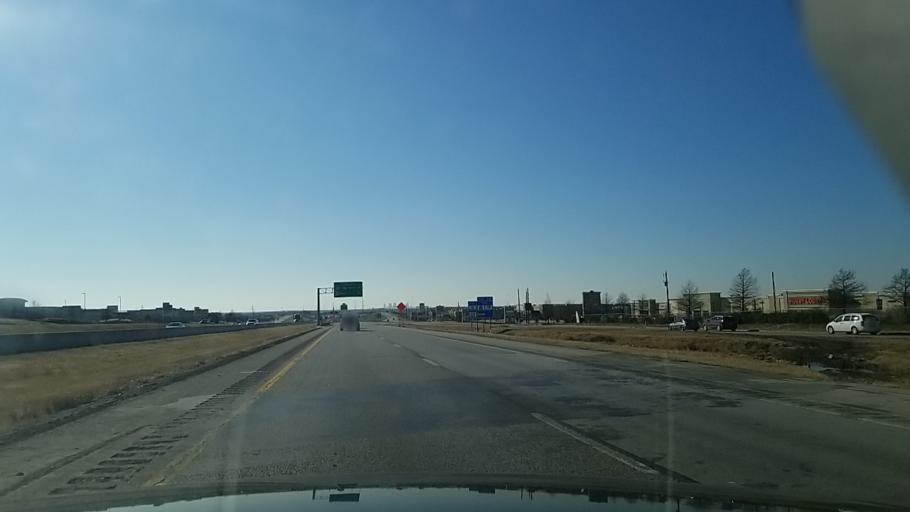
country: US
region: Texas
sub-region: Tarrant County
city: Blue Mound
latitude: 32.9088
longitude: -97.3173
